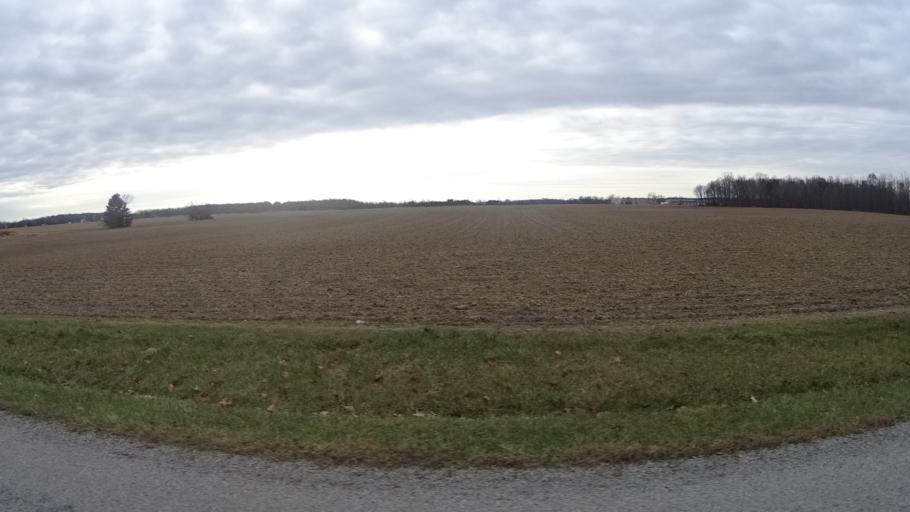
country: US
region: Ohio
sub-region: Lorain County
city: Wellington
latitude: 41.1894
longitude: -82.2024
